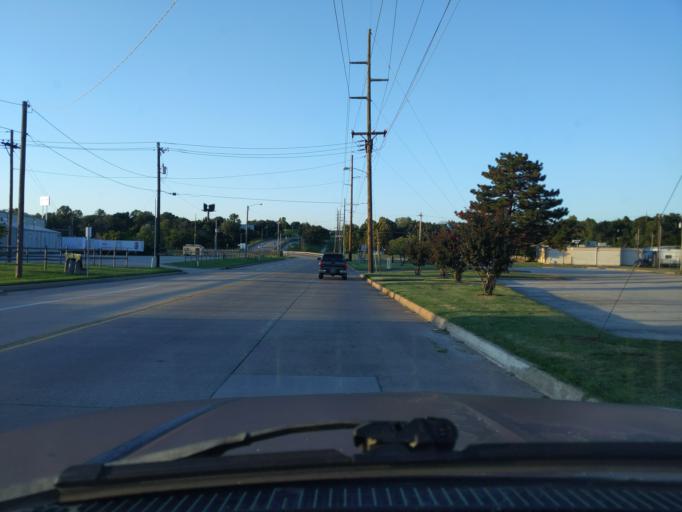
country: US
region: Oklahoma
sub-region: Tulsa County
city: Tulsa
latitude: 36.1521
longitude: -96.0203
